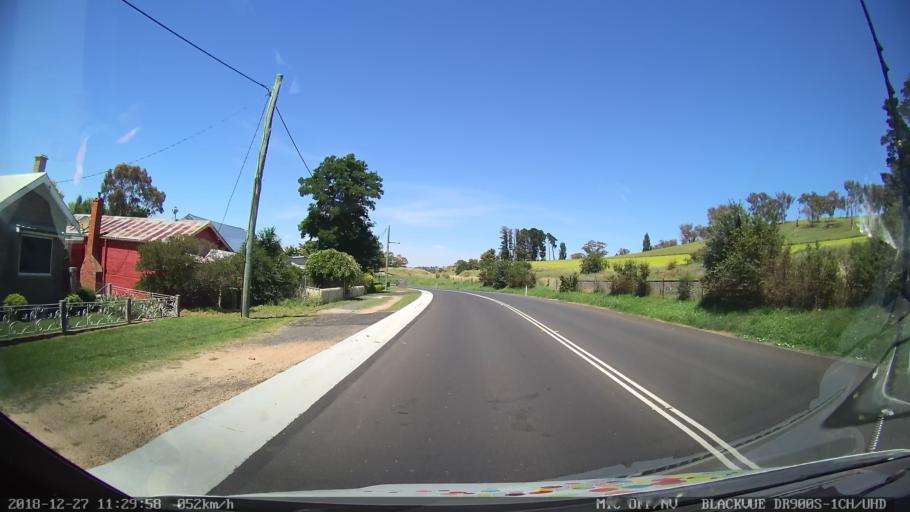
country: AU
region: New South Wales
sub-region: Bathurst Regional
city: Perthville
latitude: -33.4845
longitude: 149.5482
